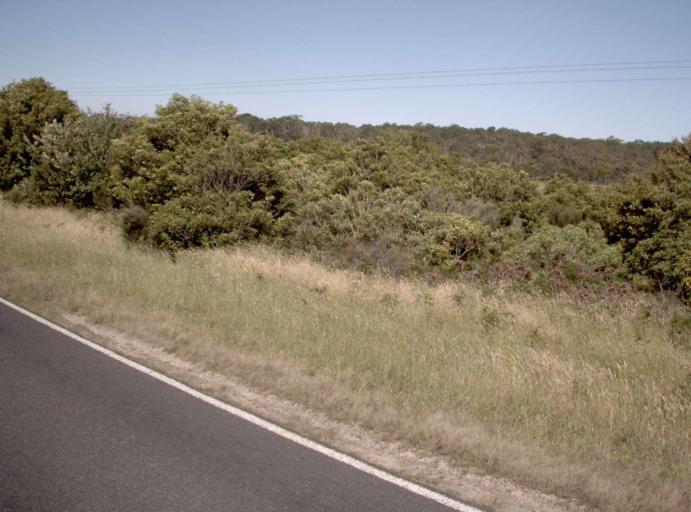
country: AU
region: Victoria
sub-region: Latrobe
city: Morwell
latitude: -38.6501
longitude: 146.4681
